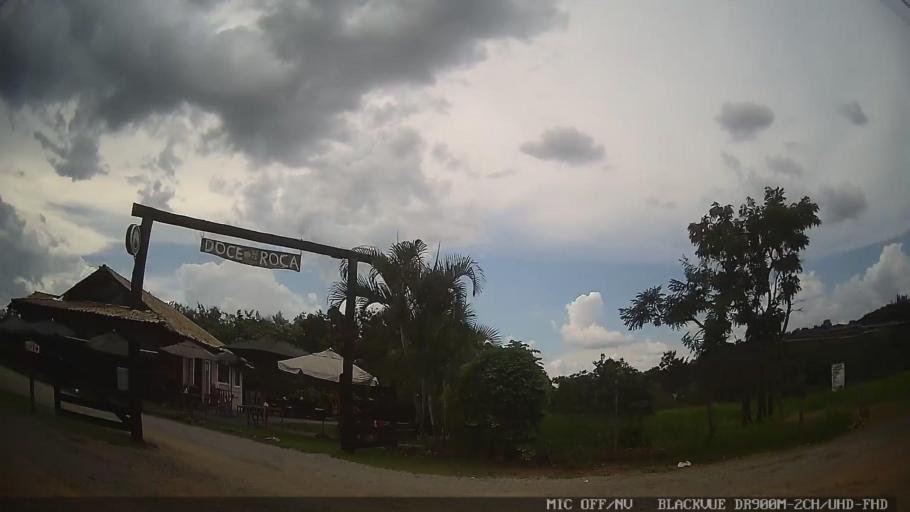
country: BR
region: Sao Paulo
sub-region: Atibaia
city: Atibaia
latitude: -23.1615
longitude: -46.5715
